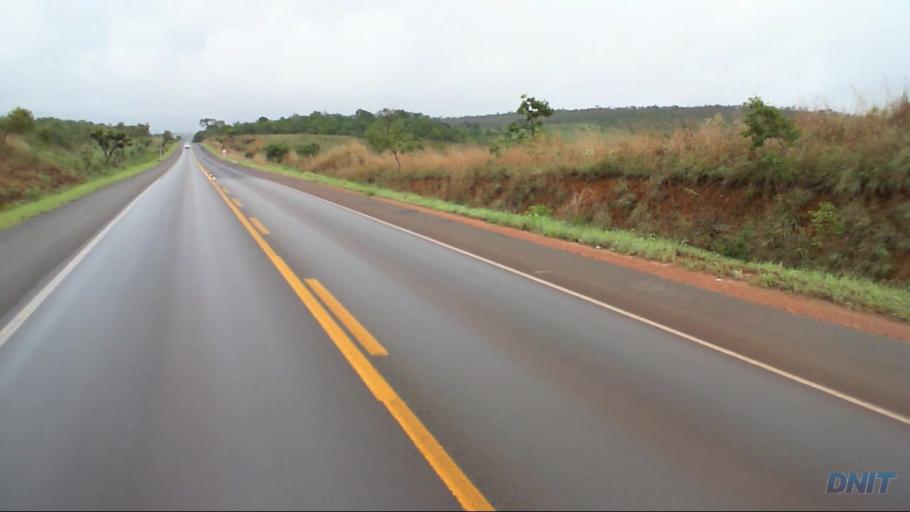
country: BR
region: Goias
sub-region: Padre Bernardo
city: Padre Bernardo
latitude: -15.2003
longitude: -48.4523
